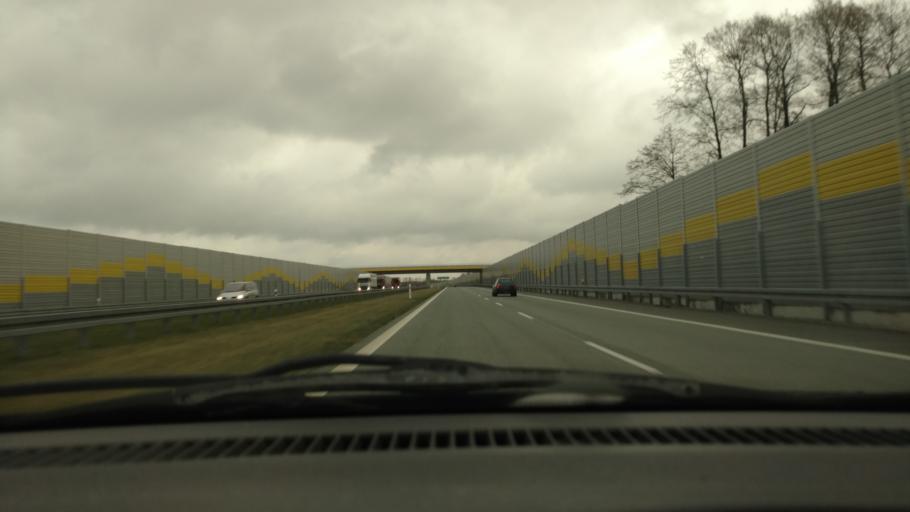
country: PL
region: Lodz Voivodeship
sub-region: Powiat pabianicki
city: Pabianice
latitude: 51.6086
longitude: 19.3363
